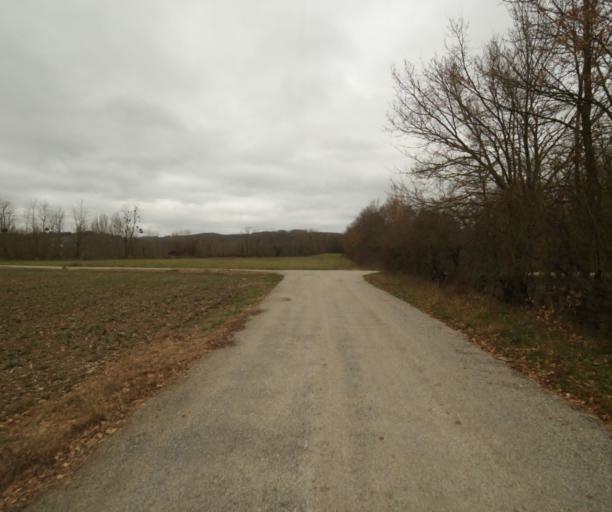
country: FR
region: Midi-Pyrenees
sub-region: Departement de l'Ariege
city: Pamiers
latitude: 43.1484
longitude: 1.5963
